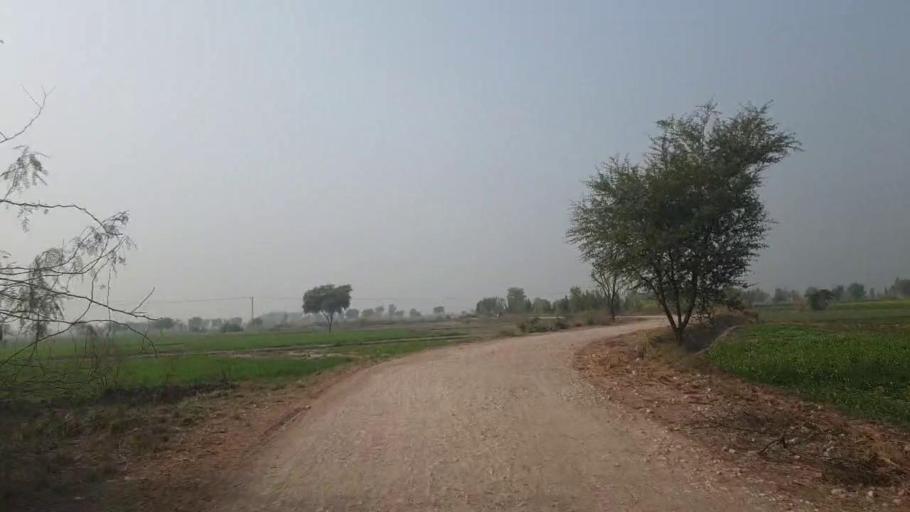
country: PK
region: Sindh
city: Bhit Shah
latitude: 25.8491
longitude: 68.5656
